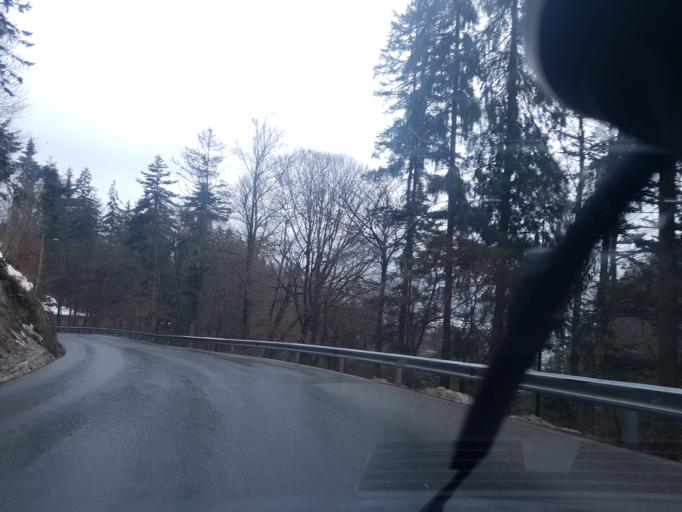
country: AT
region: Tyrol
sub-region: Politischer Bezirk Kufstein
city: Worgl
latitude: 47.4729
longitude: 12.0733
